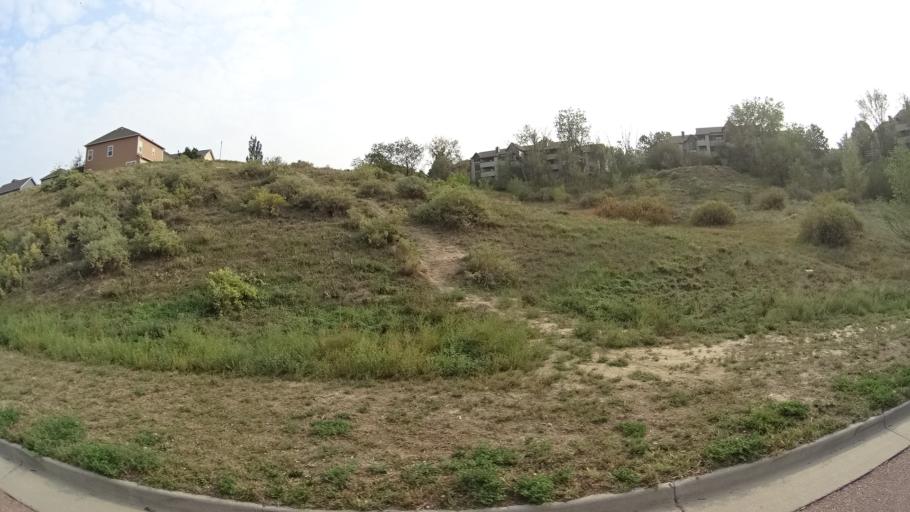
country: US
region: Colorado
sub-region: El Paso County
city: Stratmoor
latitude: 38.8051
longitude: -104.7832
